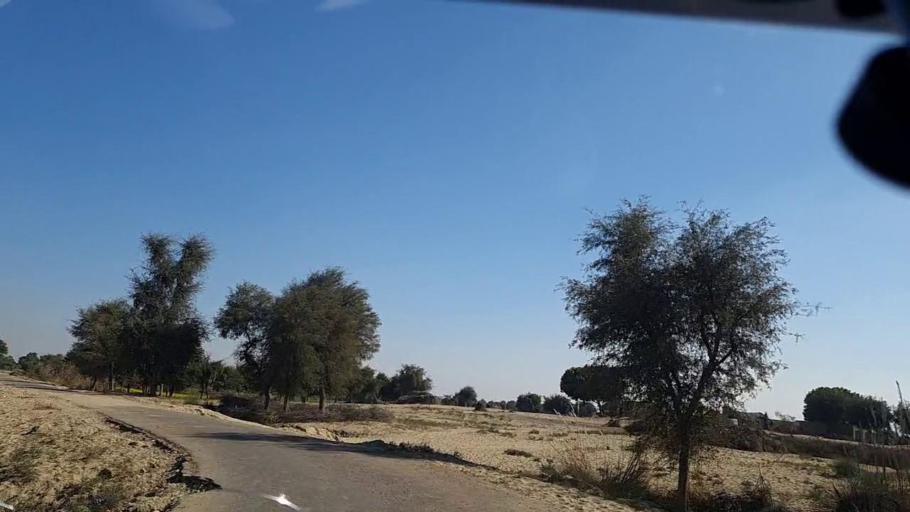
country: PK
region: Sindh
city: Khanpur
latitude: 27.6163
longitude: 69.4458
